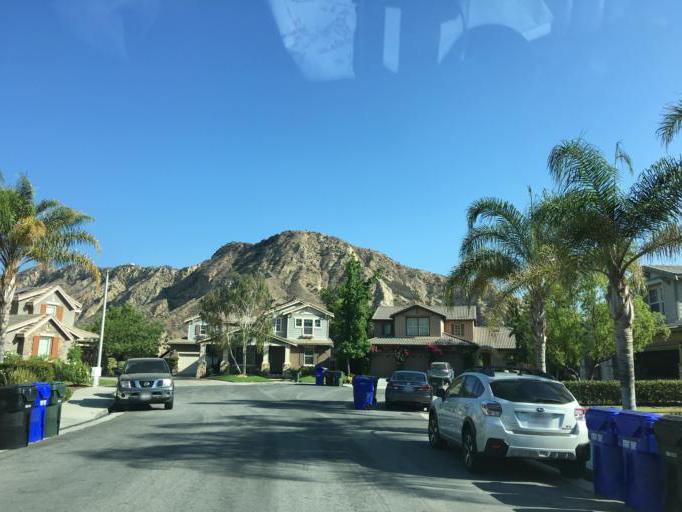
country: US
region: California
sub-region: Los Angeles County
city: Santa Clarita
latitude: 34.3751
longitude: -118.5894
